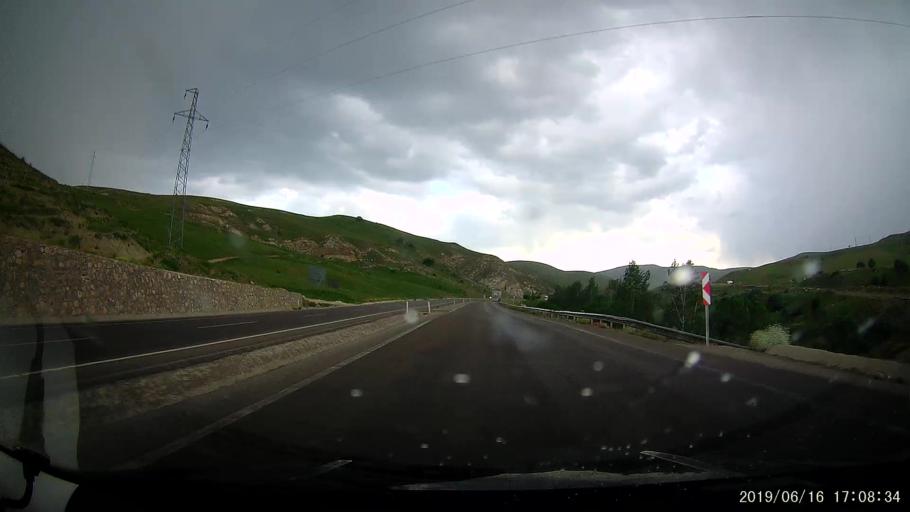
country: TR
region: Erzurum
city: Askale
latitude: 39.9070
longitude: 40.6598
